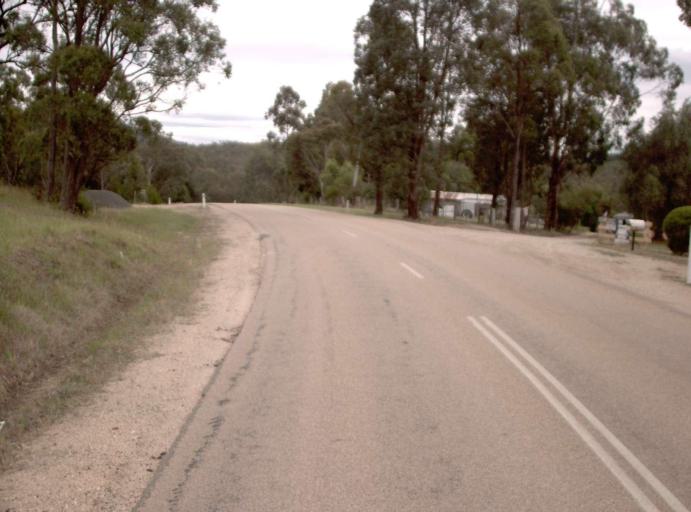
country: AU
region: Victoria
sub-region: East Gippsland
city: Bairnsdale
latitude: -37.7559
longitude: 147.5991
